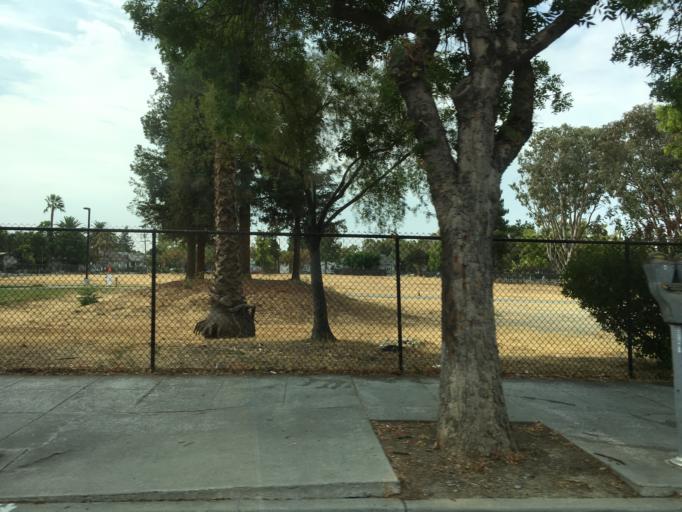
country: US
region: California
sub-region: Santa Clara County
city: San Jose
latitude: 37.3429
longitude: -121.8766
